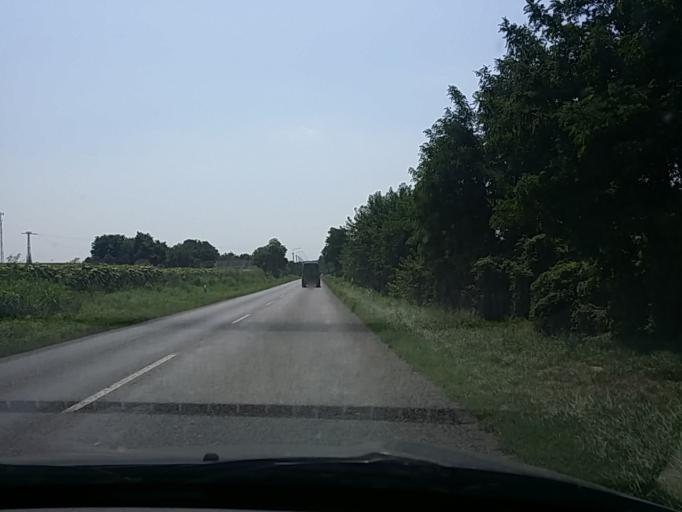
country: HU
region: Tolna
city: Iregszemcse
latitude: 46.7115
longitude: 18.1754
